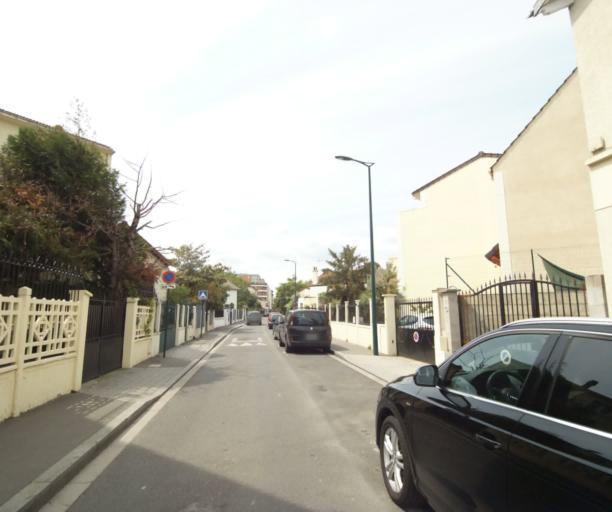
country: FR
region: Ile-de-France
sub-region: Departement des Hauts-de-Seine
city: Bois-Colombes
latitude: 48.9298
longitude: 2.2706
